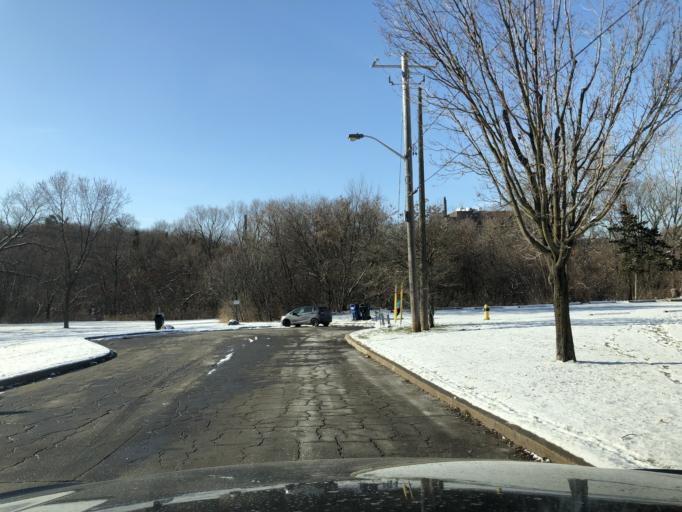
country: CA
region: Ontario
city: Etobicoke
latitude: 43.7105
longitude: -79.5379
